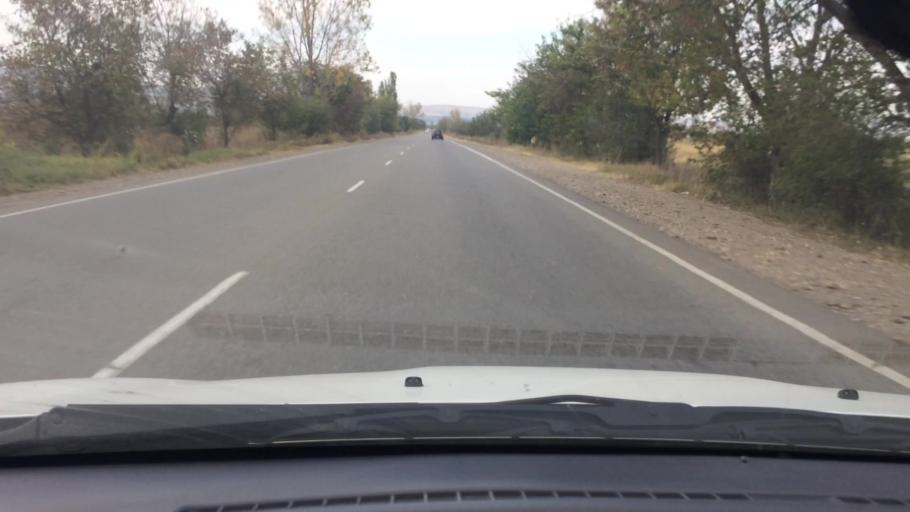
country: GE
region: Kvemo Kartli
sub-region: Marneuli
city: Marneuli
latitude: 41.5539
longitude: 44.7763
